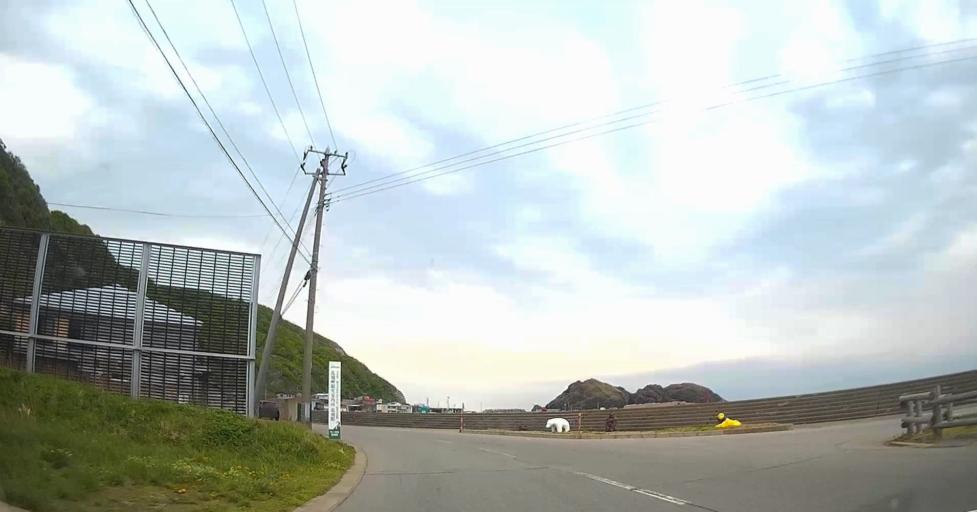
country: JP
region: Aomori
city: Shimokizukuri
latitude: 41.2581
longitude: 140.3487
